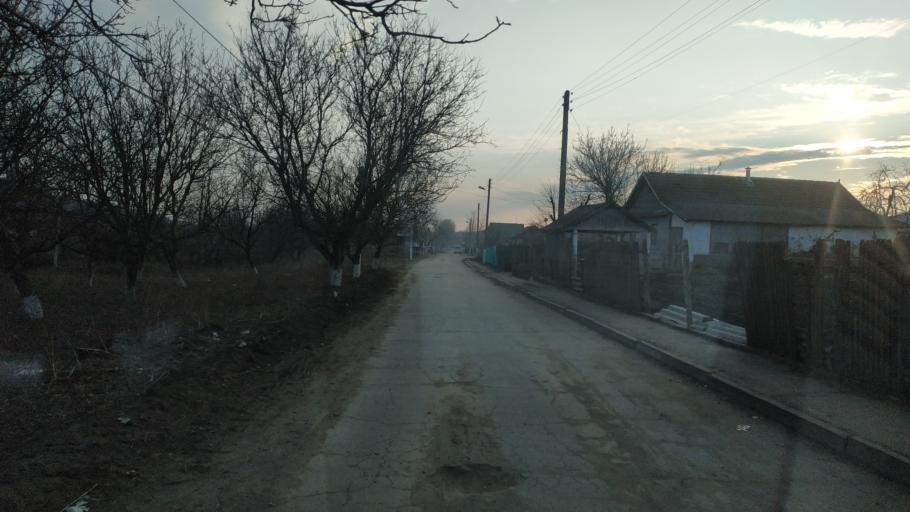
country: MD
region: Hincesti
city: Dancu
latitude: 46.7153
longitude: 28.3499
